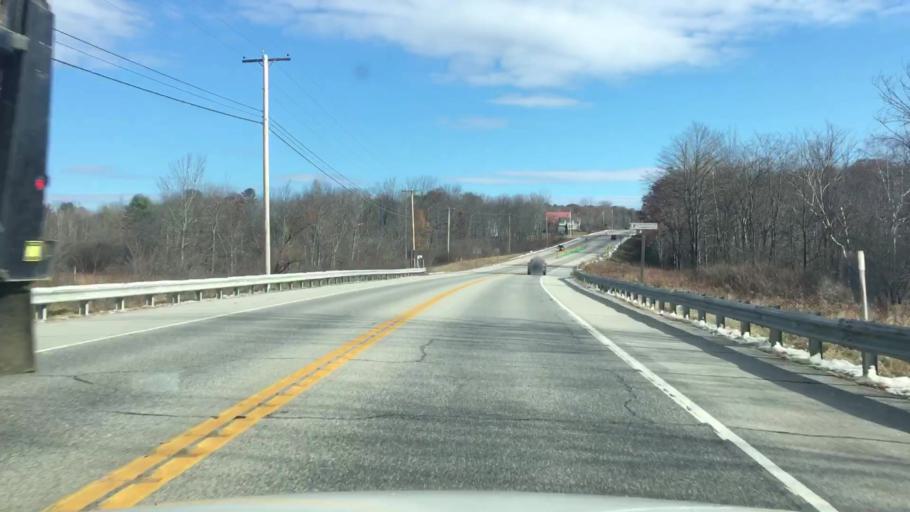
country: US
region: Maine
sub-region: Kennebec County
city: Winthrop
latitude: 44.3190
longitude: -69.9324
